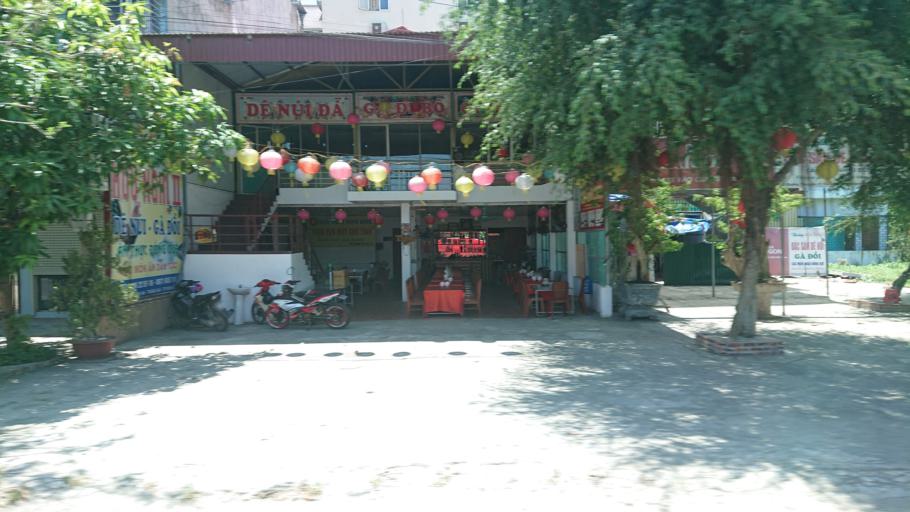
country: VN
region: Ninh Binh
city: Thanh Pho Ninh Binh
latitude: 20.2636
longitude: 105.9631
